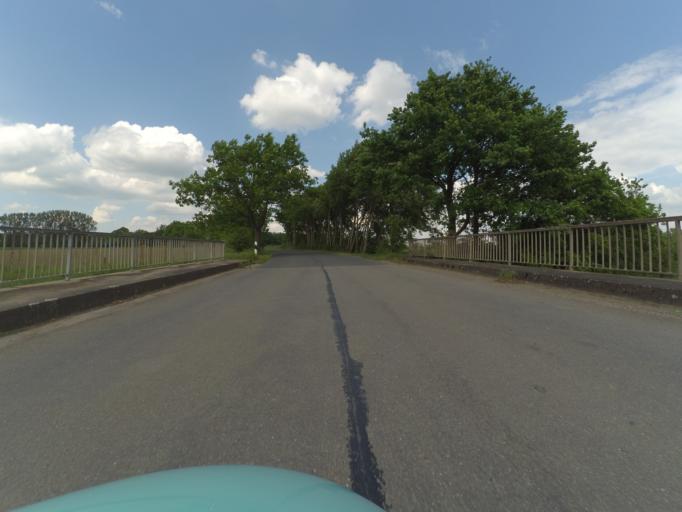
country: DE
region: Lower Saxony
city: Lehrte
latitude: 52.3698
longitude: 10.0272
